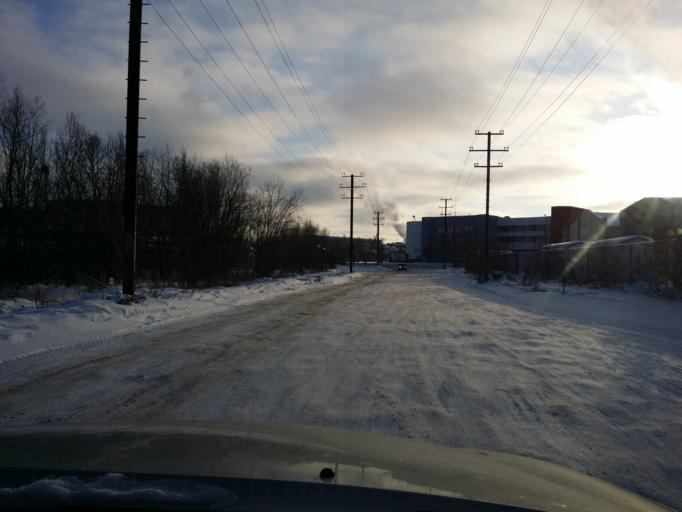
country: RU
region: Khanty-Mansiyskiy Avtonomnyy Okrug
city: Megion
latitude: 61.0425
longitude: 76.1028
